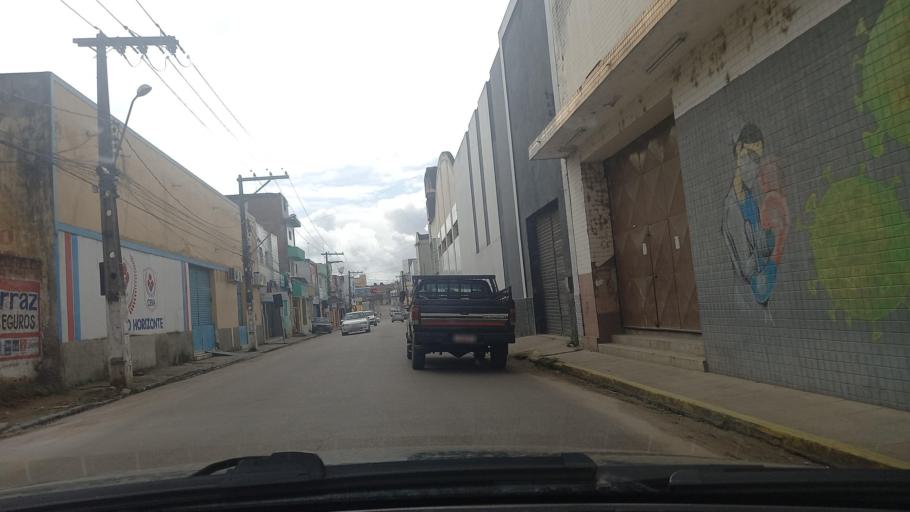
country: BR
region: Pernambuco
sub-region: Vitoria De Santo Antao
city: Vitoria de Santo Antao
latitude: -8.1181
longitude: -35.2980
